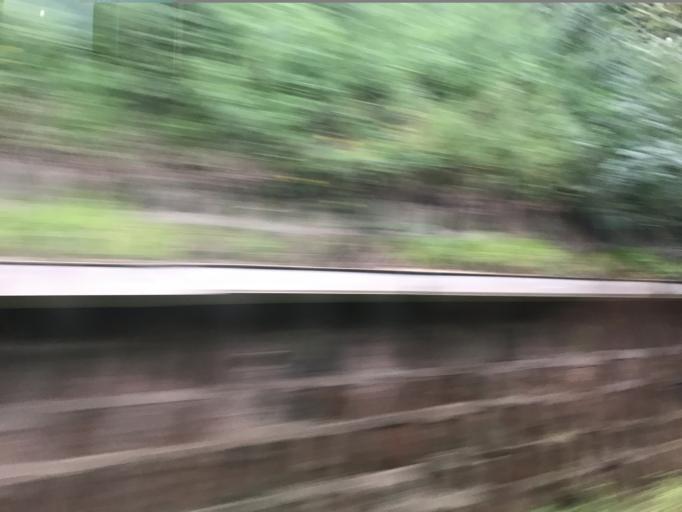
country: VA
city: Vatican City
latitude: 41.8452
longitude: 12.4544
